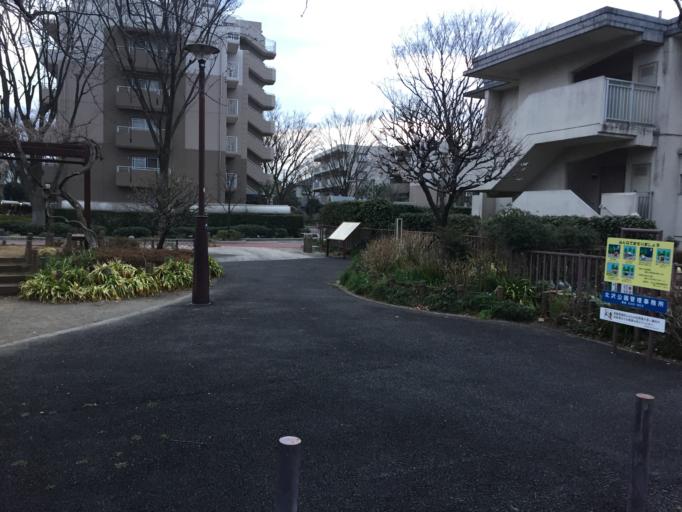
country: JP
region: Tokyo
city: Tokyo
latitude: 35.6591
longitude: 139.6336
